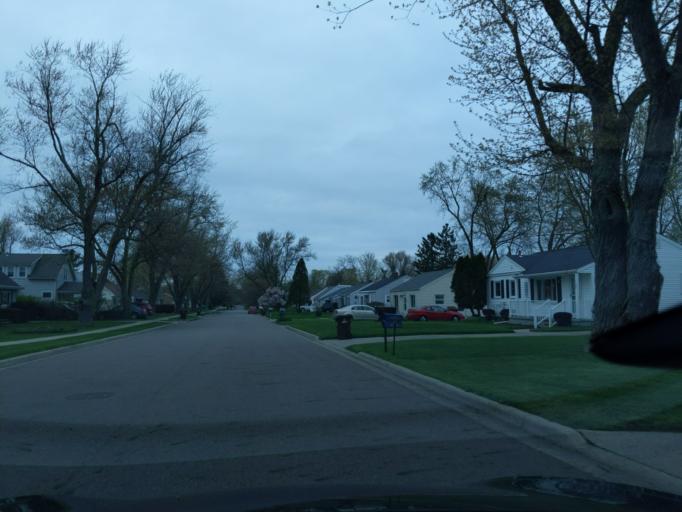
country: US
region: Michigan
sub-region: Eaton County
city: Waverly
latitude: 42.7347
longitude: -84.6146
